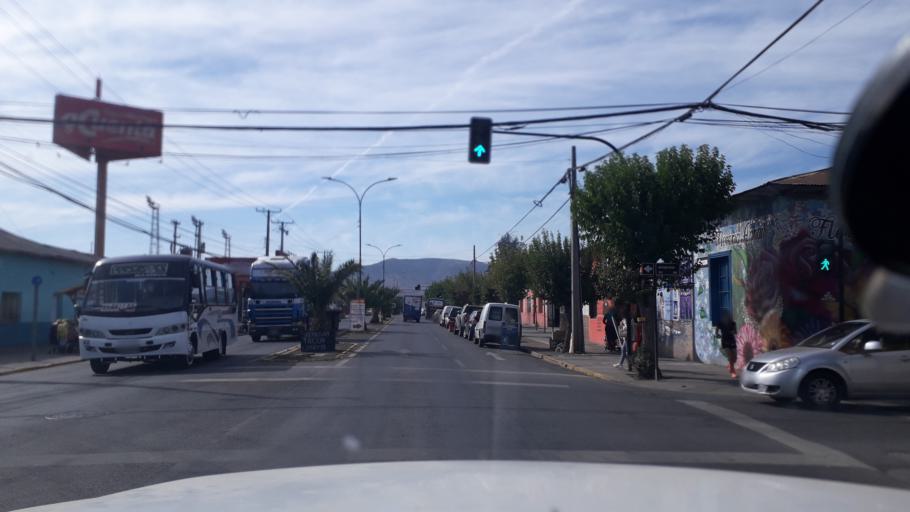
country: CL
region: Valparaiso
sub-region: Provincia de San Felipe
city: San Felipe
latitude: -32.7491
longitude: -70.7296
